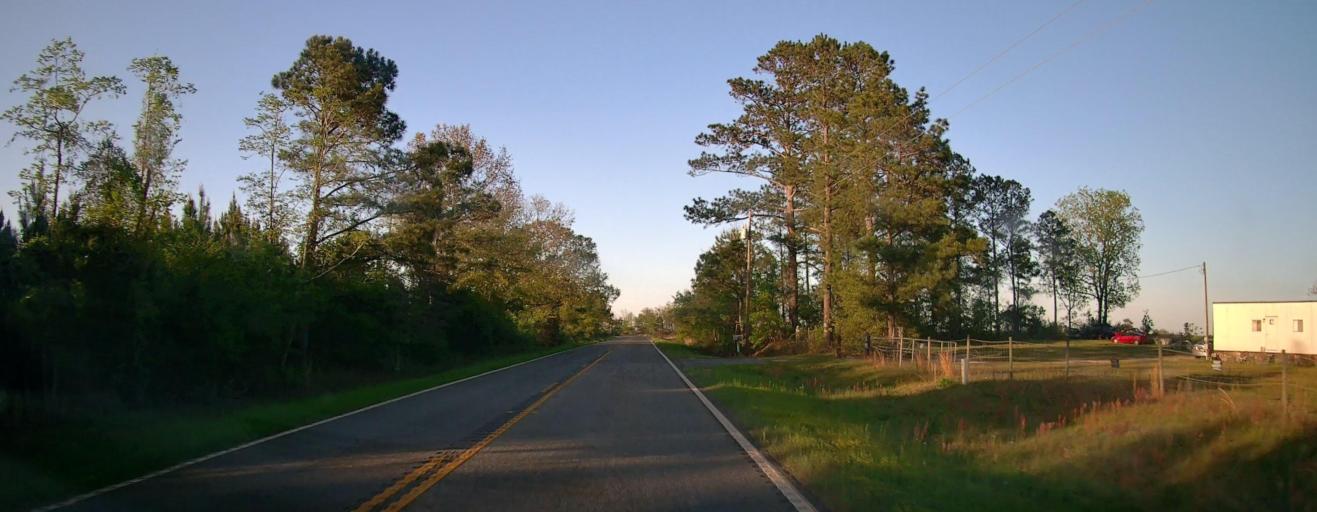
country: US
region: Georgia
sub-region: Marion County
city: Buena Vista
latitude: 32.4276
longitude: -84.4301
